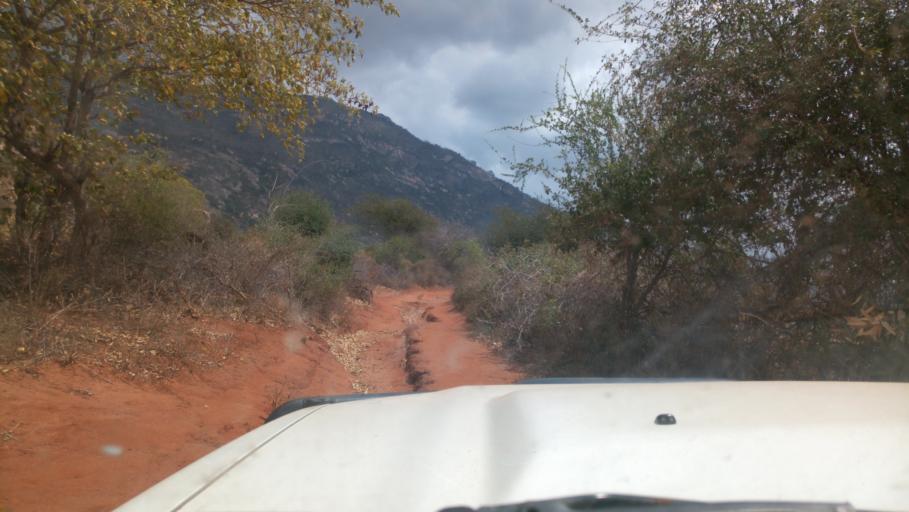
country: KE
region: Kitui
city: Kitui
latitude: -1.8839
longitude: 38.3727
